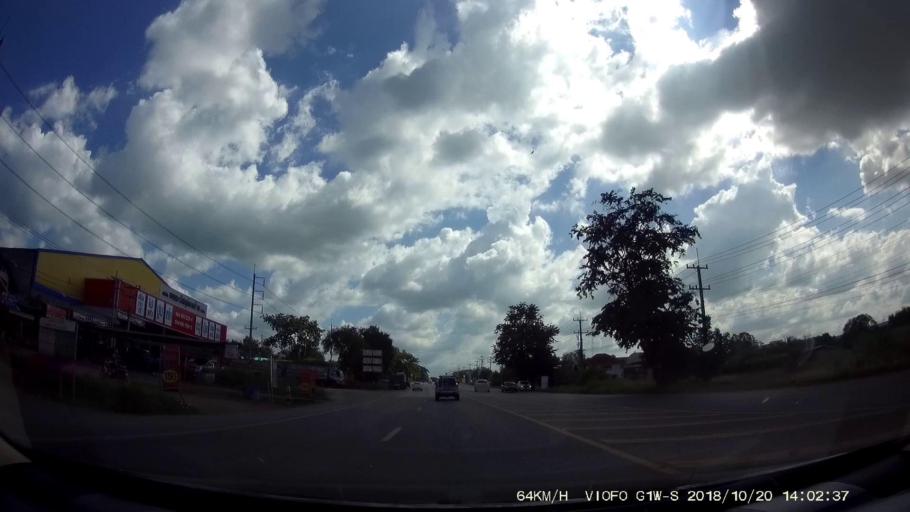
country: TH
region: Khon Kaen
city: Chum Phae
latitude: 16.4898
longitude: 102.1247
